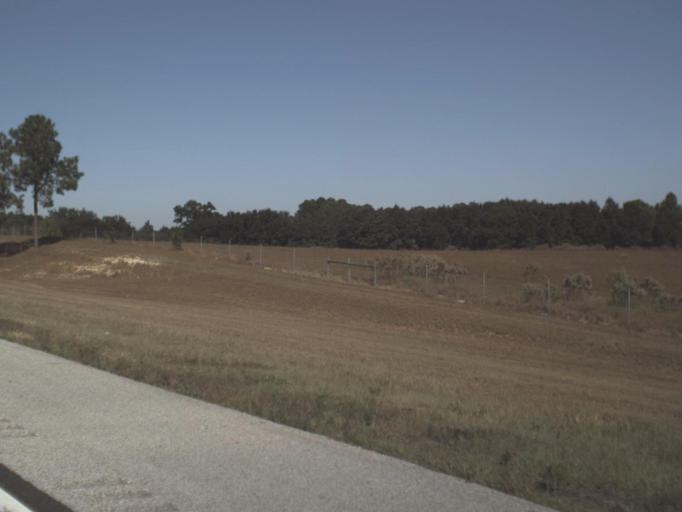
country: US
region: Florida
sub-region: Lake County
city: Hawthorne
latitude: 28.7028
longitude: -81.8832
